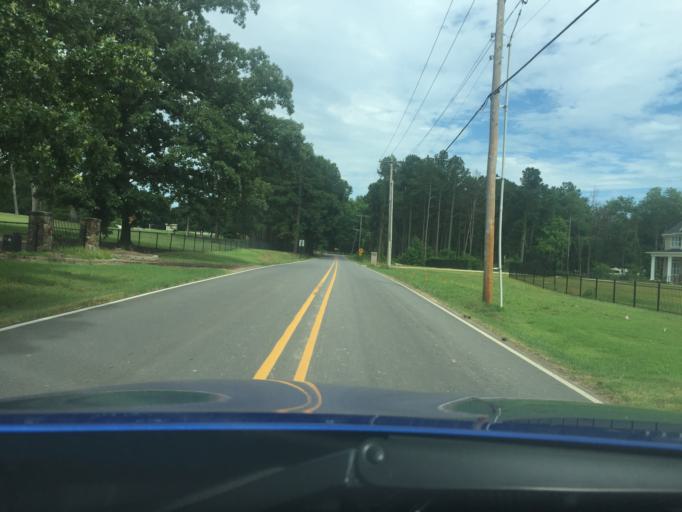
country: US
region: Arkansas
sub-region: Pulaski County
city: Maumelle
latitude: 34.8302
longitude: -92.4385
